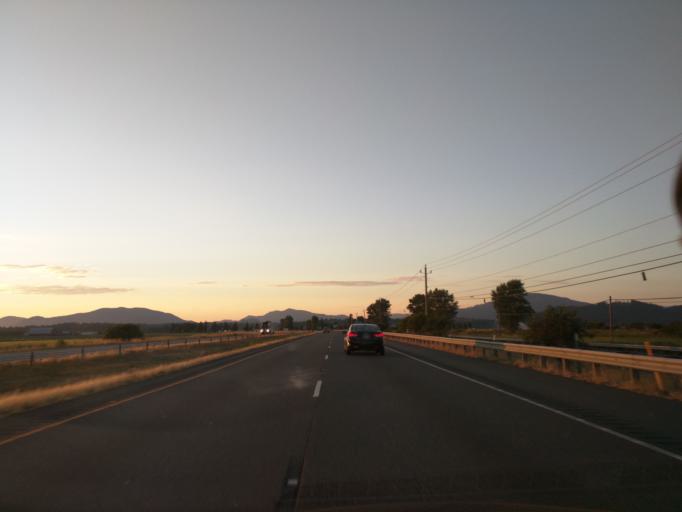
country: US
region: Washington
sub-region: Skagit County
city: Burlington
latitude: 48.4940
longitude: -122.3353
